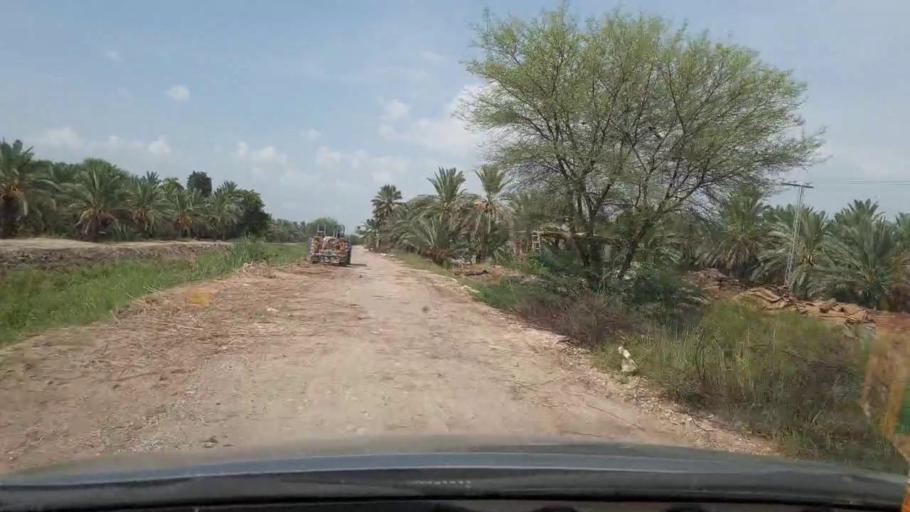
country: PK
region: Sindh
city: Khairpur
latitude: 27.5176
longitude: 68.8820
